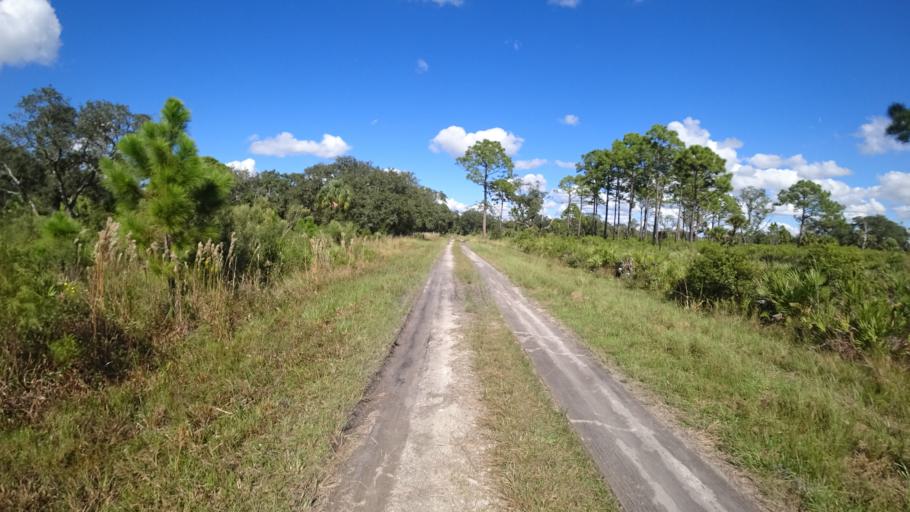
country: US
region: Florida
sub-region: Sarasota County
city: Lake Sarasota
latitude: 27.2527
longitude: -82.2796
